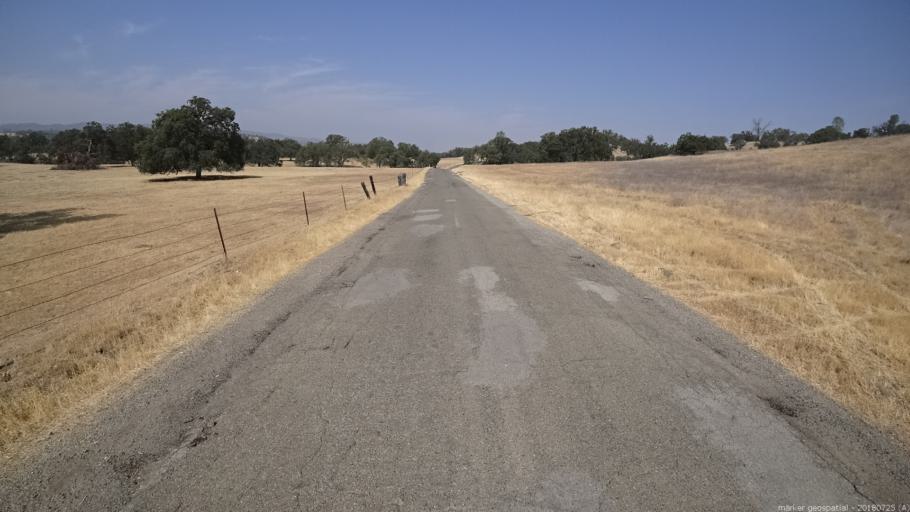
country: US
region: California
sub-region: San Luis Obispo County
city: Shandon
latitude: 35.8756
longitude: -120.4149
